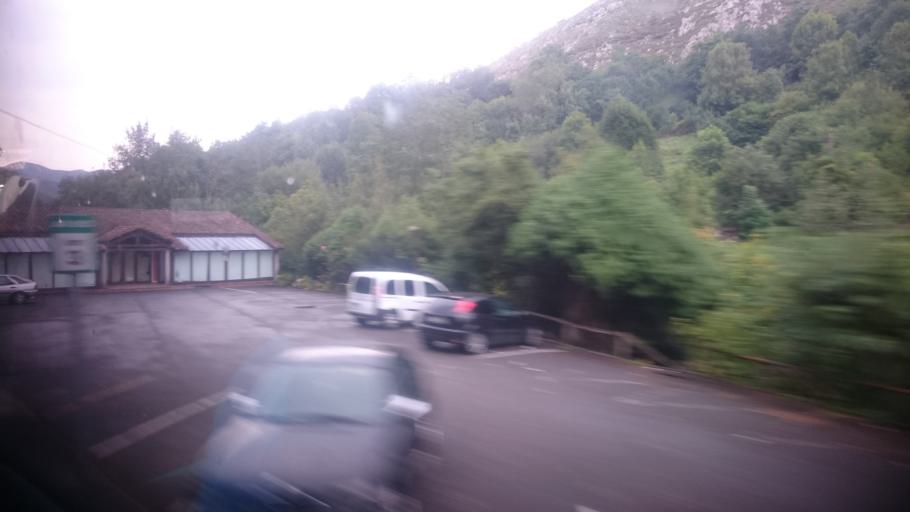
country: ES
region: Asturias
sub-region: Province of Asturias
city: Cangas de Onis
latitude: 43.3222
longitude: -5.0766
